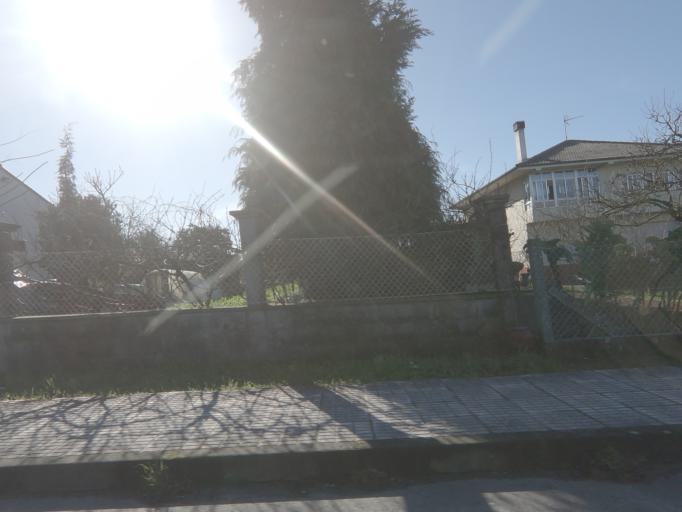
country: ES
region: Galicia
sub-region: Provincia de Pontevedra
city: Silleda
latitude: 42.6835
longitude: -8.1929
